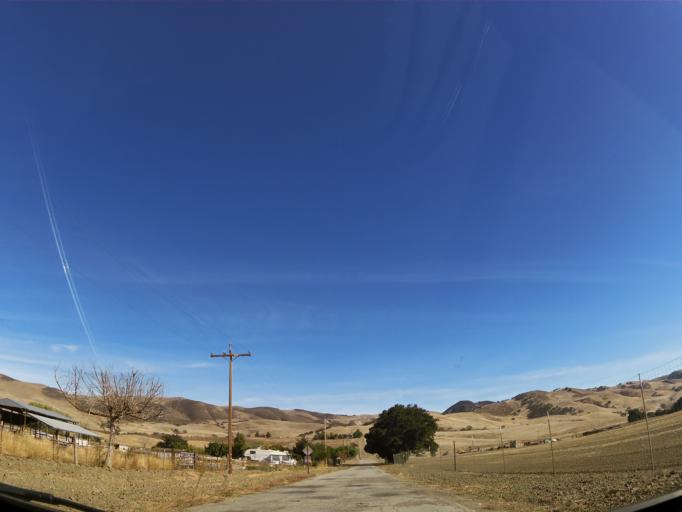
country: US
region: California
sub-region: San Benito County
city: Ridgemark
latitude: 36.6662
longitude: -121.2533
